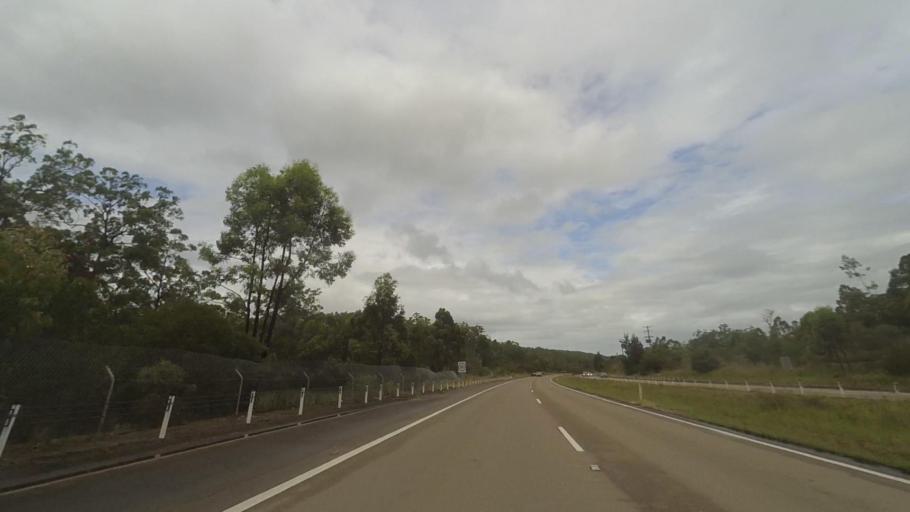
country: AU
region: New South Wales
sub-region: Port Stephens Shire
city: Medowie
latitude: -32.6241
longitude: 151.9475
